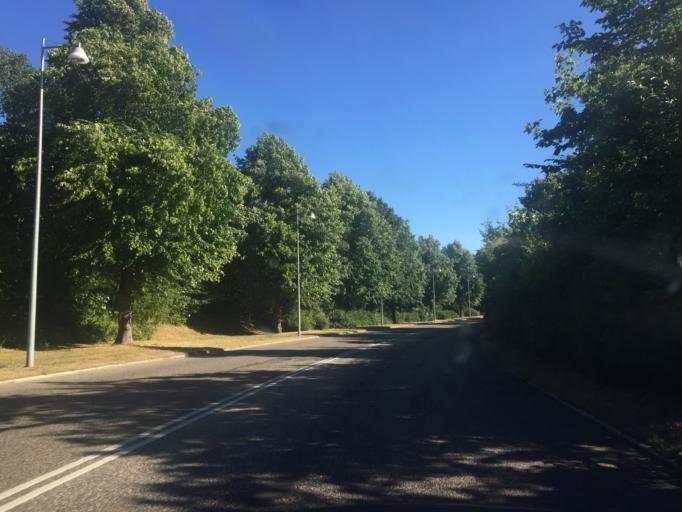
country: DK
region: Capital Region
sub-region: Albertslund Kommune
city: Albertslund
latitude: 55.6767
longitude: 12.3438
